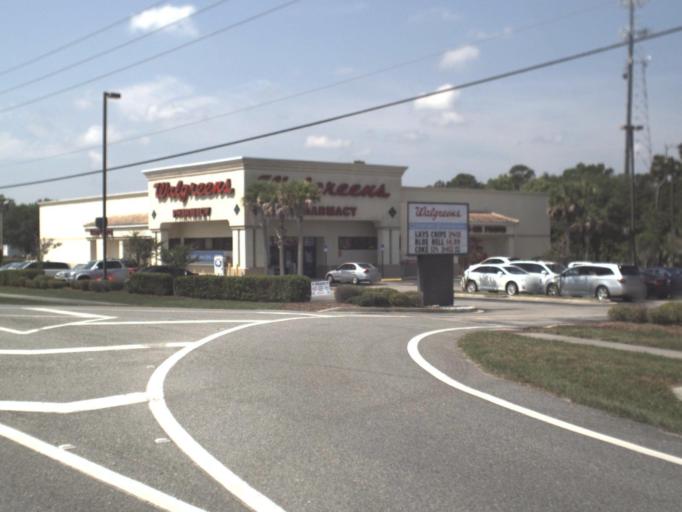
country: US
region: Florida
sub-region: Saint Johns County
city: Sawgrass
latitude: 30.1939
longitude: -81.3806
